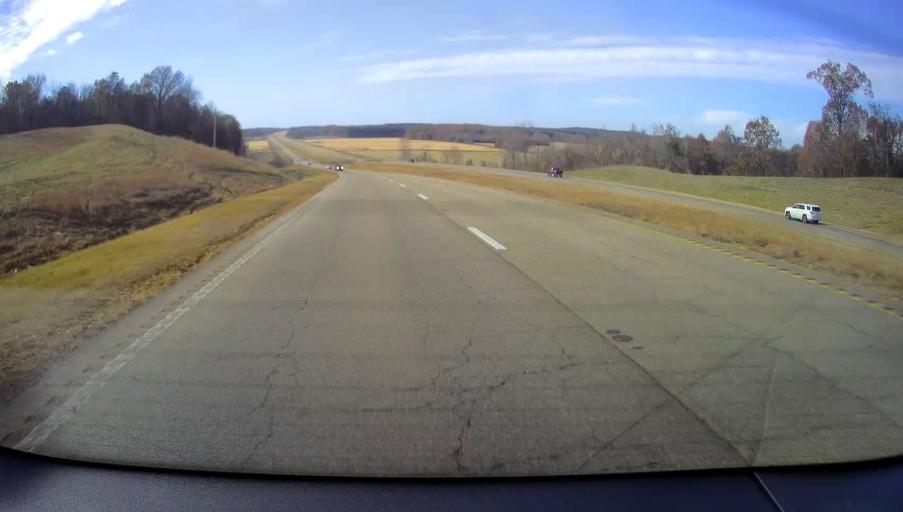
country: US
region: Mississippi
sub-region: Alcorn County
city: Corinth
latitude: 34.9324
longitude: -88.6477
